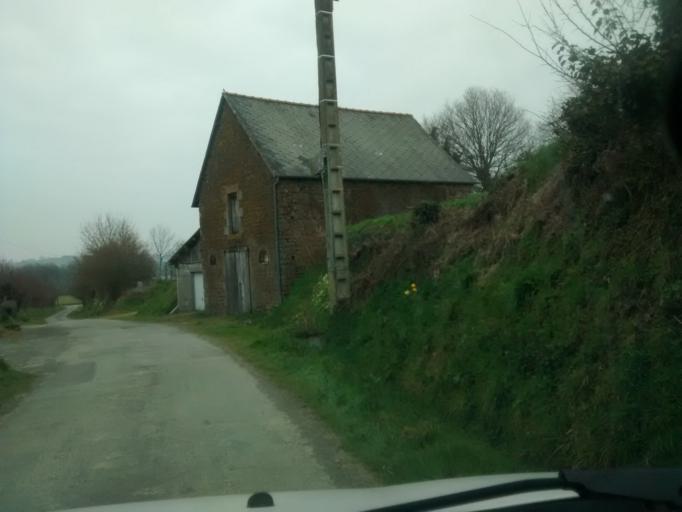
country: FR
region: Brittany
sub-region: Departement d'Ille-et-Vilaine
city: Bazouges-la-Perouse
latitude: 48.3983
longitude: -1.5901
